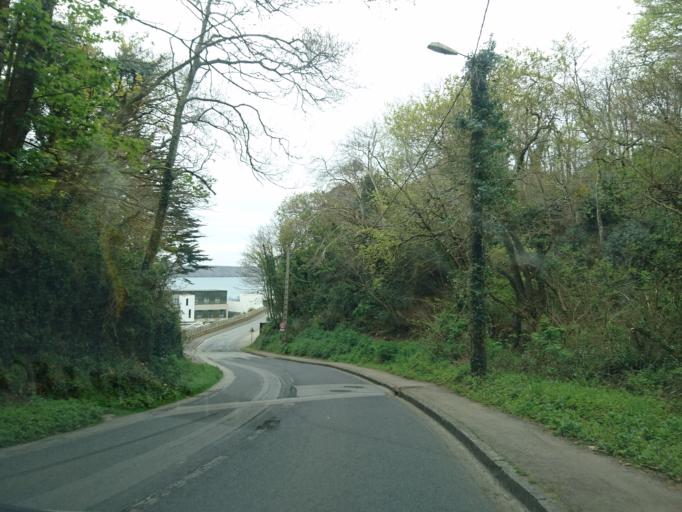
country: FR
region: Brittany
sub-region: Departement du Finistere
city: Roscanvel
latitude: 48.3637
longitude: -4.5504
